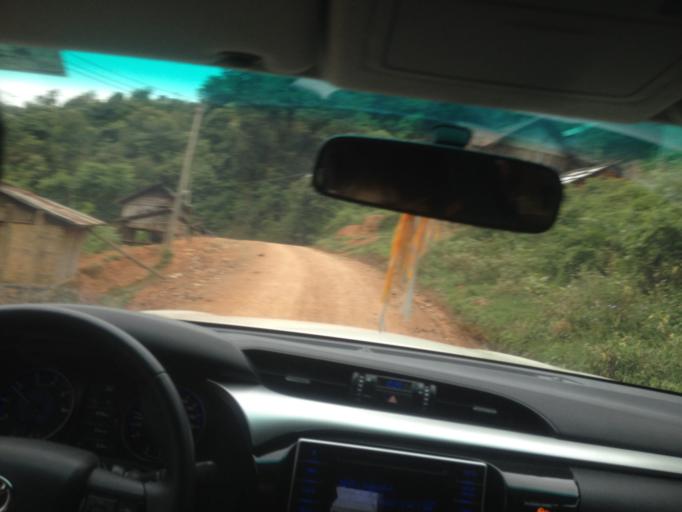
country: TH
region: Nan
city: Chaloem Phra Kiat
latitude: 19.9753
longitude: 101.1359
